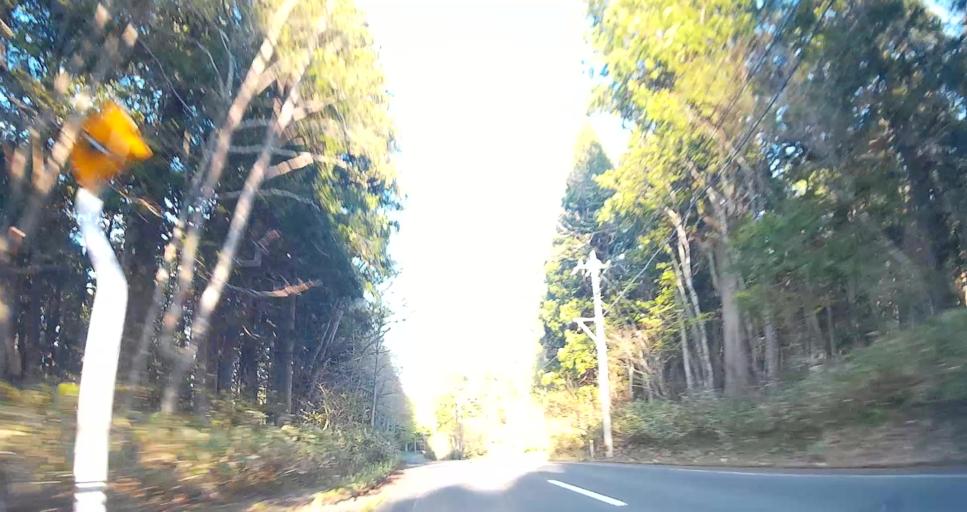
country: JP
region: Aomori
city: Mutsu
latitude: 41.3151
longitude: 141.1189
